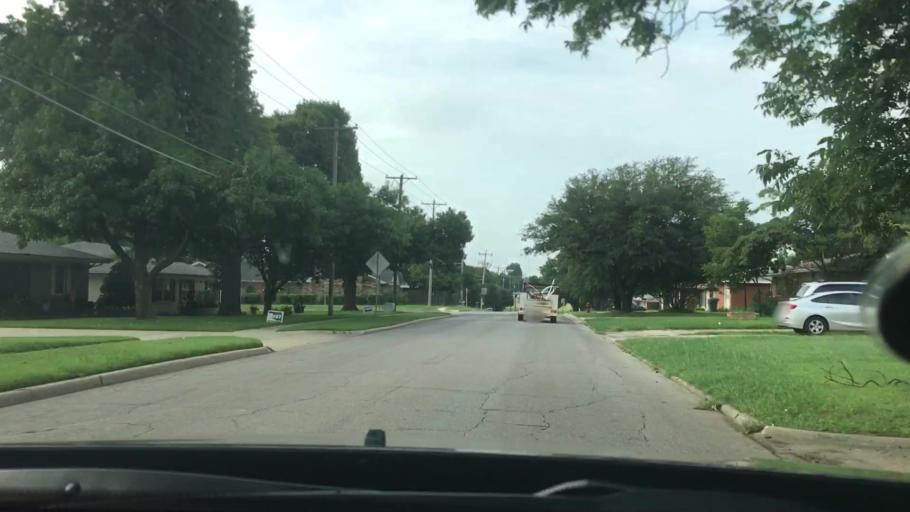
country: US
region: Oklahoma
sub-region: Carter County
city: Ardmore
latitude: 34.1940
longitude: -97.1255
